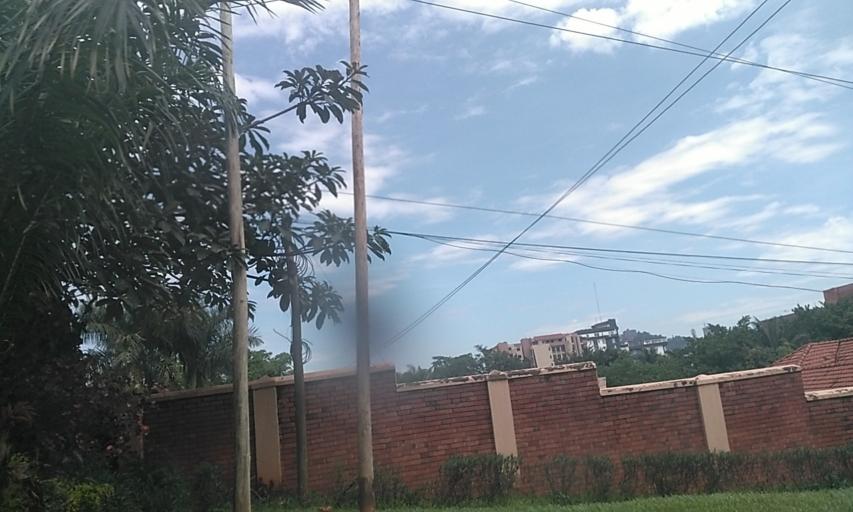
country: UG
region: Central Region
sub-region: Kampala District
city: Kampala
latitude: 0.3271
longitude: 32.6002
